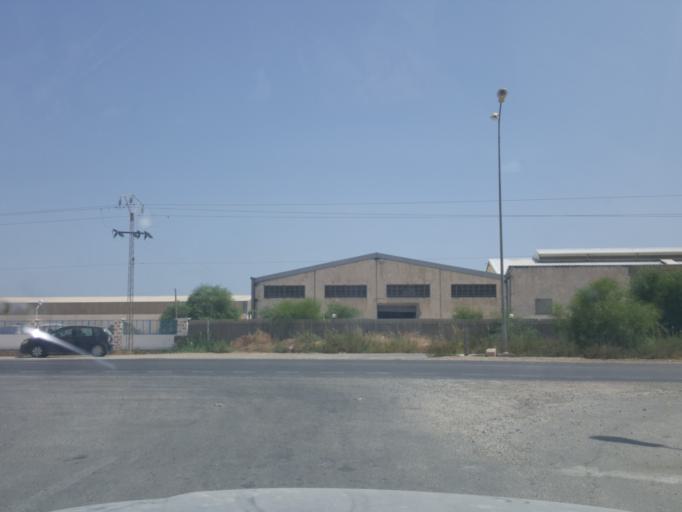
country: TN
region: Qabis
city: Gabes
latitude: 33.9812
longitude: 10.0058
